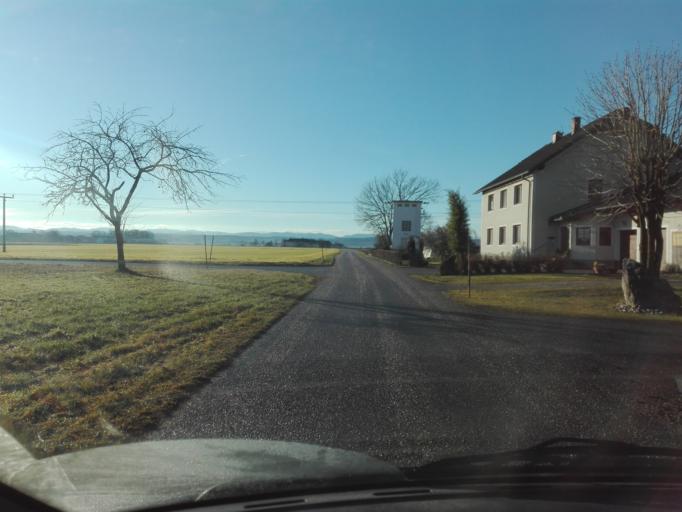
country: AT
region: Upper Austria
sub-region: Politischer Bezirk Perg
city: Perg
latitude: 48.2024
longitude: 14.6763
